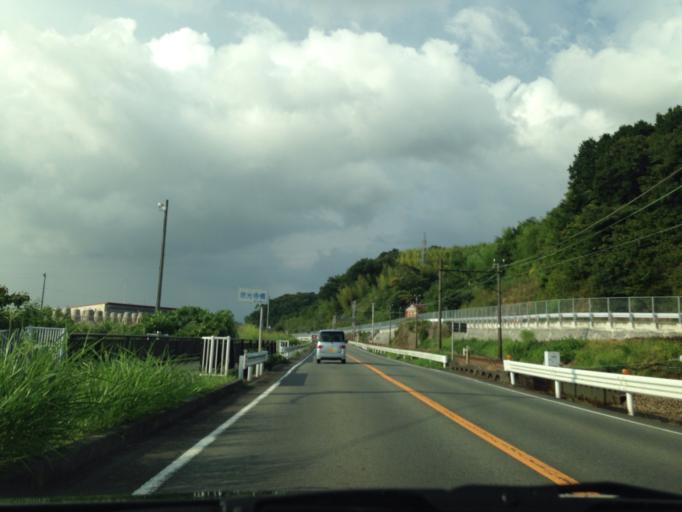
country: JP
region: Shizuoka
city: Mishima
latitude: 35.0282
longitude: 138.9486
